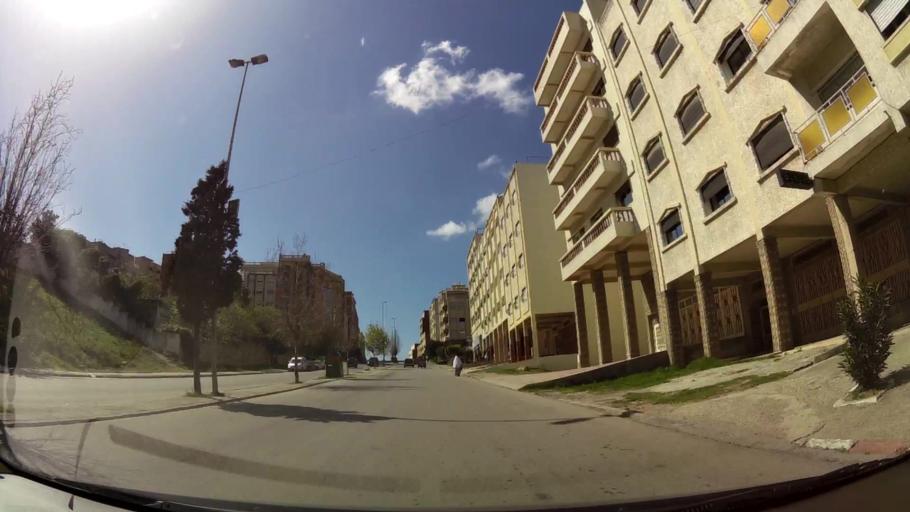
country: MA
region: Tanger-Tetouan
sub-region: Tanger-Assilah
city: Tangier
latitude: 35.7502
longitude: -5.8148
